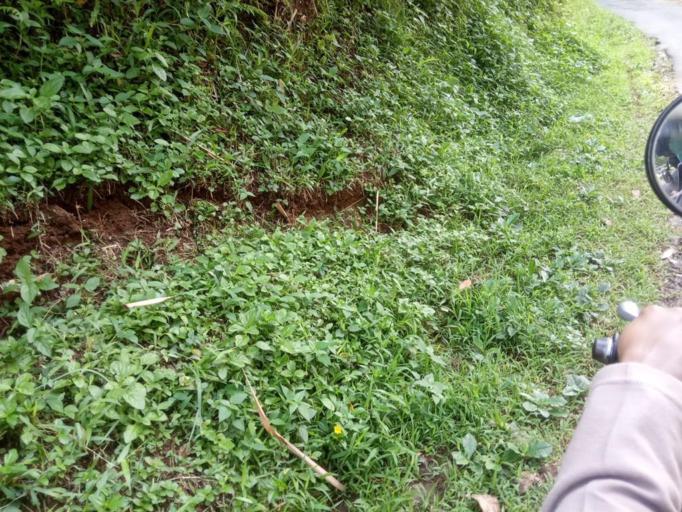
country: ID
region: West Java
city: Caringin
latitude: -6.6632
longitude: 106.8801
